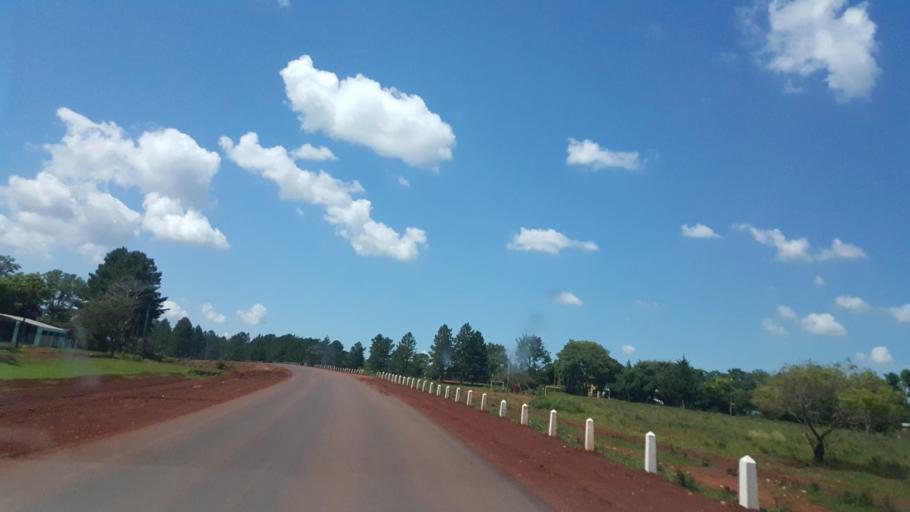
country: AR
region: Corrientes
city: Santo Tome
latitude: -28.5090
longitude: -56.0597
